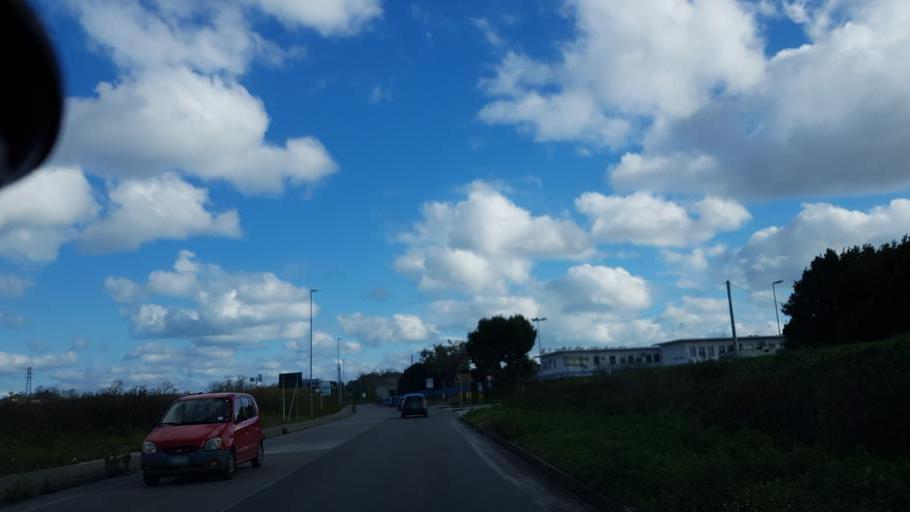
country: IT
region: Apulia
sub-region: Provincia di Brindisi
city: Brindisi
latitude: 40.6266
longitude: 17.9154
